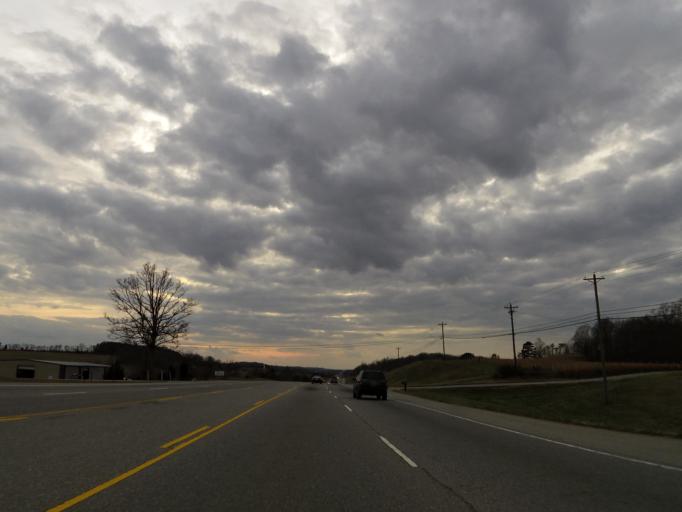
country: US
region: Tennessee
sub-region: Blount County
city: Maryville
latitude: 35.6874
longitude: -84.0578
